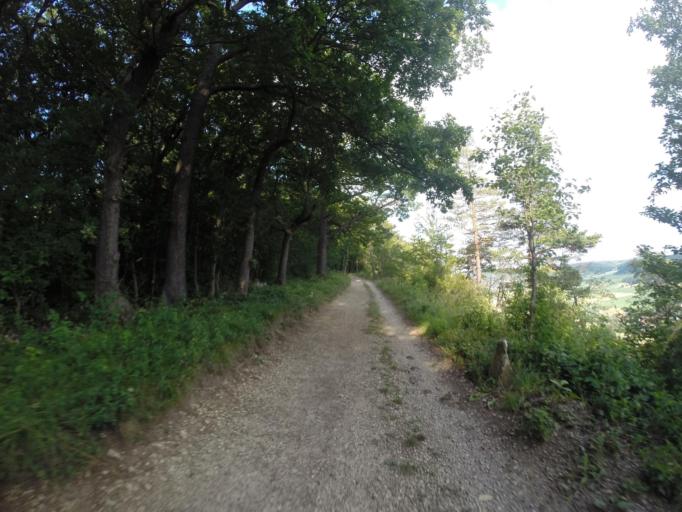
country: DE
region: Thuringia
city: Golmsdorf
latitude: 50.9383
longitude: 11.6500
